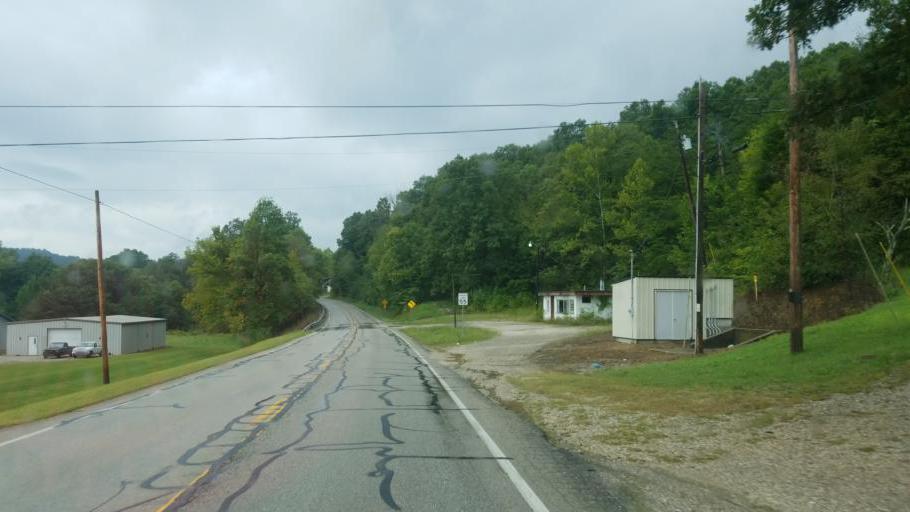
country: US
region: Kentucky
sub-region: Rowan County
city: Morehead
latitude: 38.1563
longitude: -83.4674
